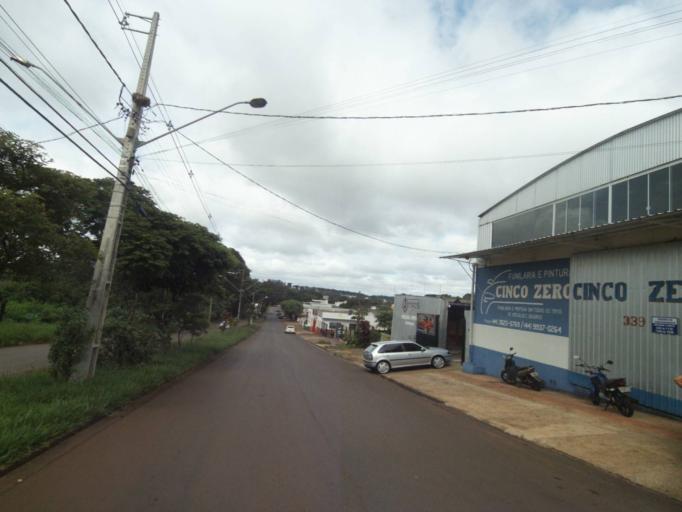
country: BR
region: Parana
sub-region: Campo Mourao
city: Campo Mourao
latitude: -24.0516
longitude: -52.3802
